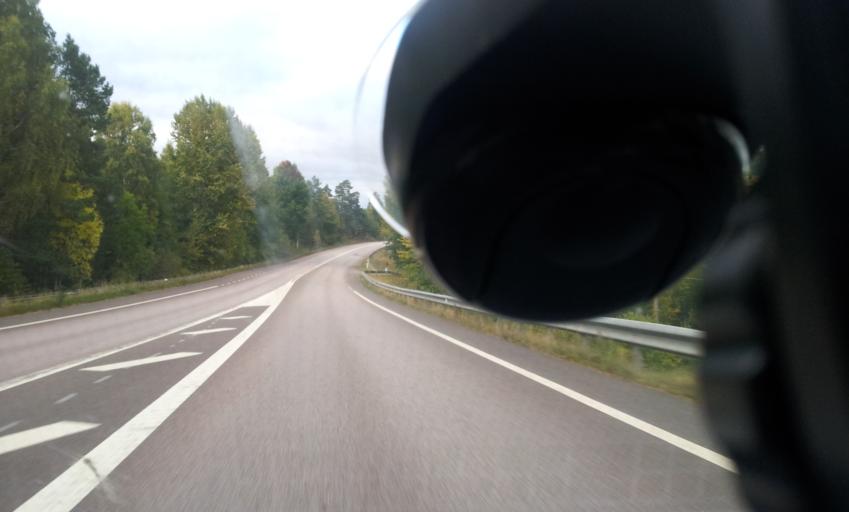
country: SE
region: Kalmar
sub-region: Oskarshamns Kommun
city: Oskarshamn
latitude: 57.4254
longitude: 16.4829
